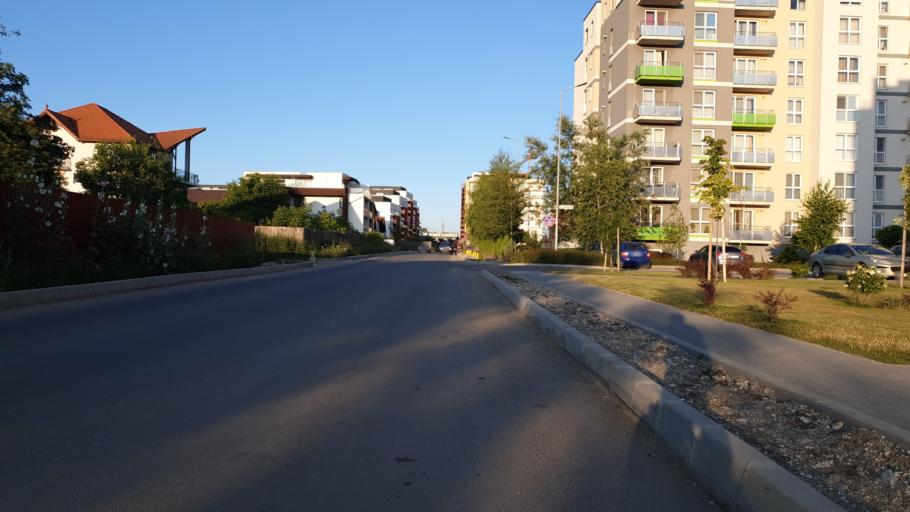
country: RO
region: Brasov
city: Brasov
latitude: 45.6751
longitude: 25.6061
